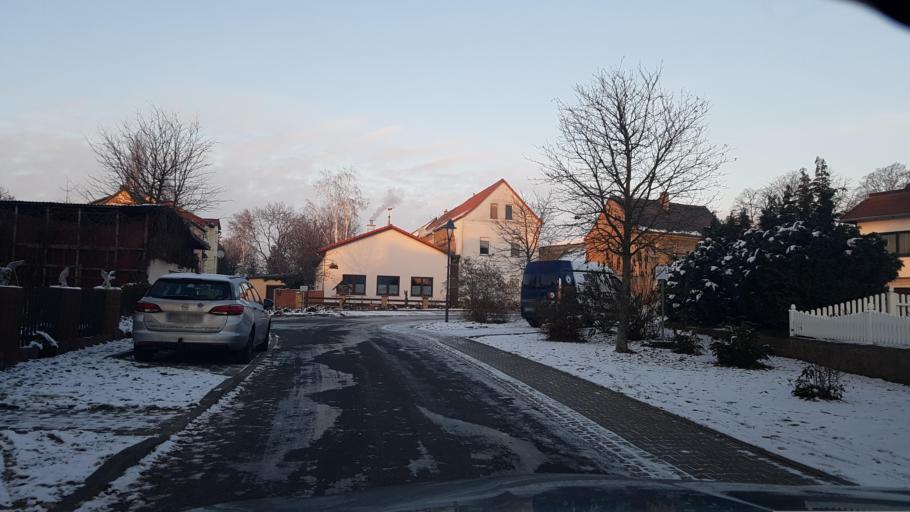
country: DE
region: Saxony
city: Jesewitz
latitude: 51.4360
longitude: 12.5138
